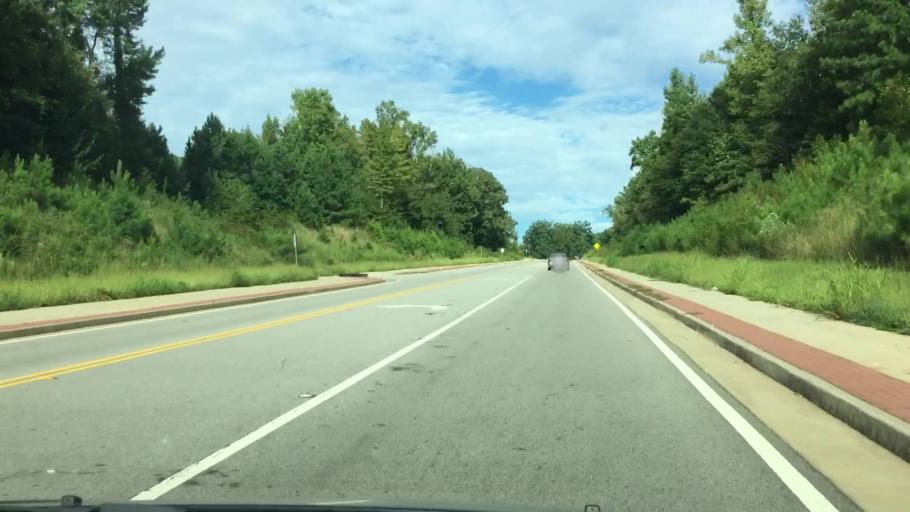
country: US
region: Georgia
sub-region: Clayton County
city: Conley
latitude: 33.6474
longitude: -84.2716
